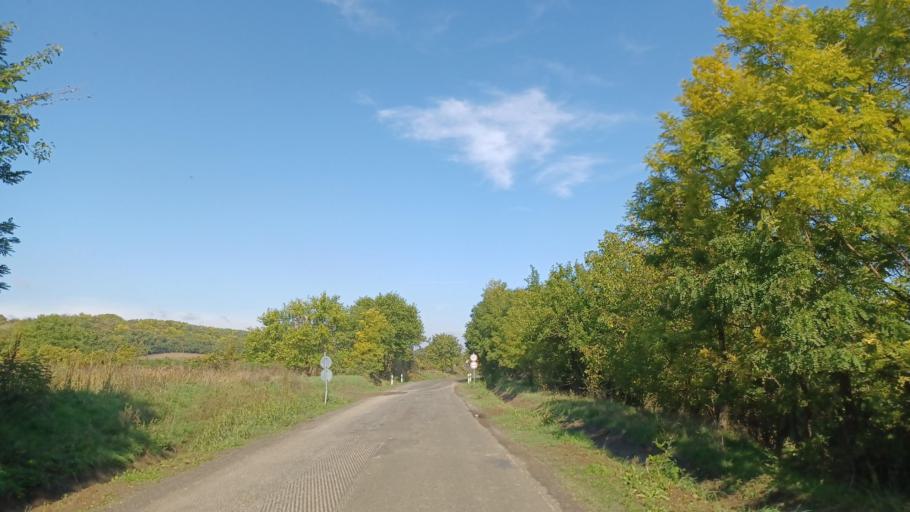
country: HU
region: Tolna
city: Nagydorog
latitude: 46.5920
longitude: 18.5962
